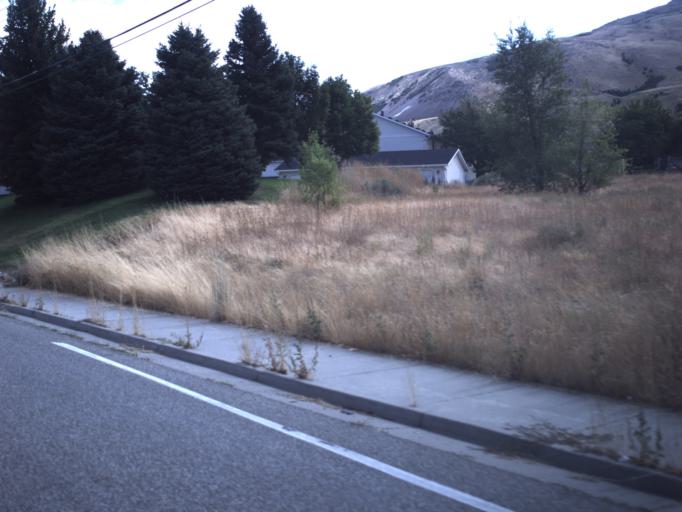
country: US
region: Utah
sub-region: Box Elder County
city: Perry
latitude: 41.4773
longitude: -112.0231
